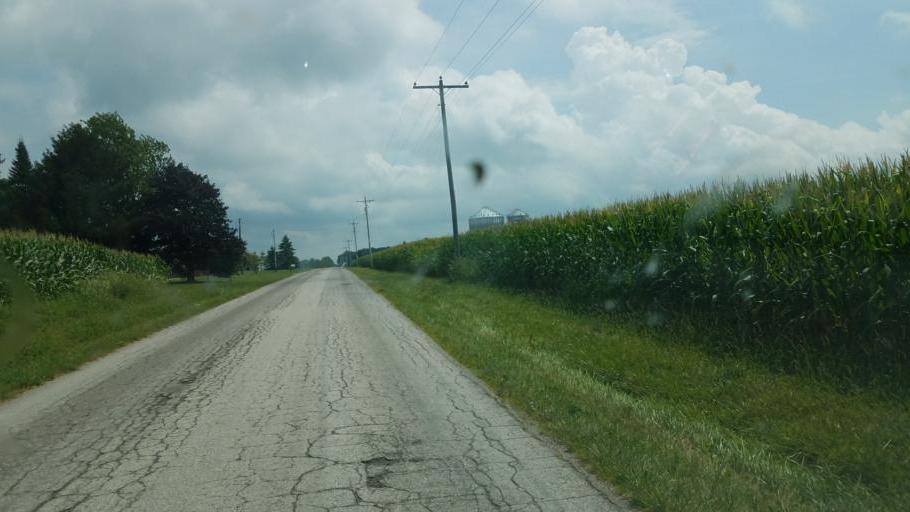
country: US
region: Ohio
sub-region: Morrow County
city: Mount Gilead
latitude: 40.6019
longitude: -82.7245
